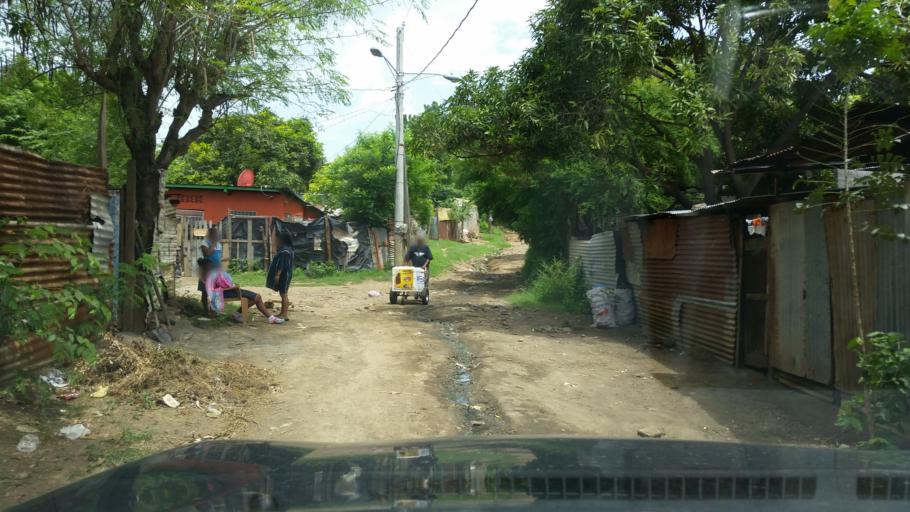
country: NI
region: Managua
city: Managua
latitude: 12.1164
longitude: -86.2211
